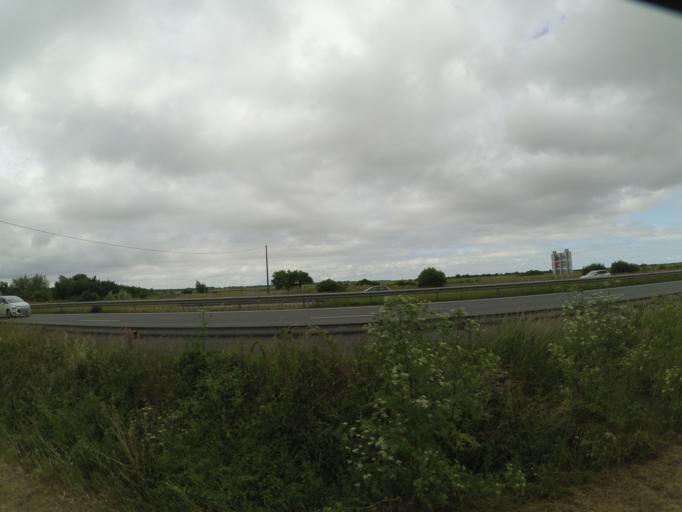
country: FR
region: Poitou-Charentes
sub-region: Departement de la Charente-Maritime
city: Yves
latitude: 46.0035
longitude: -1.0440
